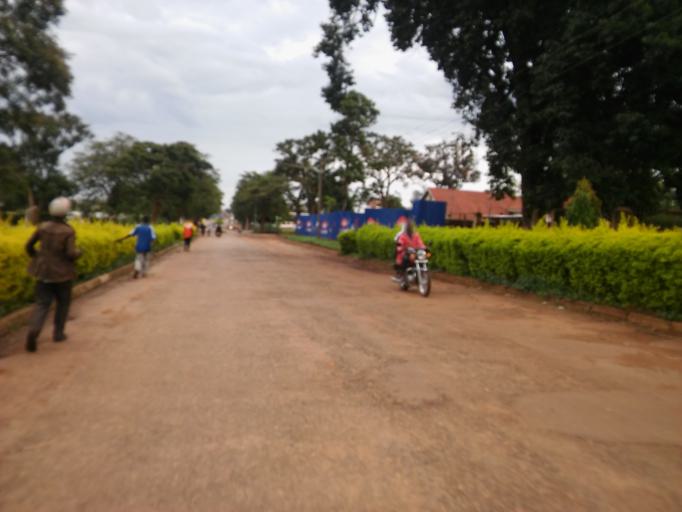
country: UG
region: Eastern Region
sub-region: Mbale District
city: Mbale
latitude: 1.0683
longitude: 34.1830
